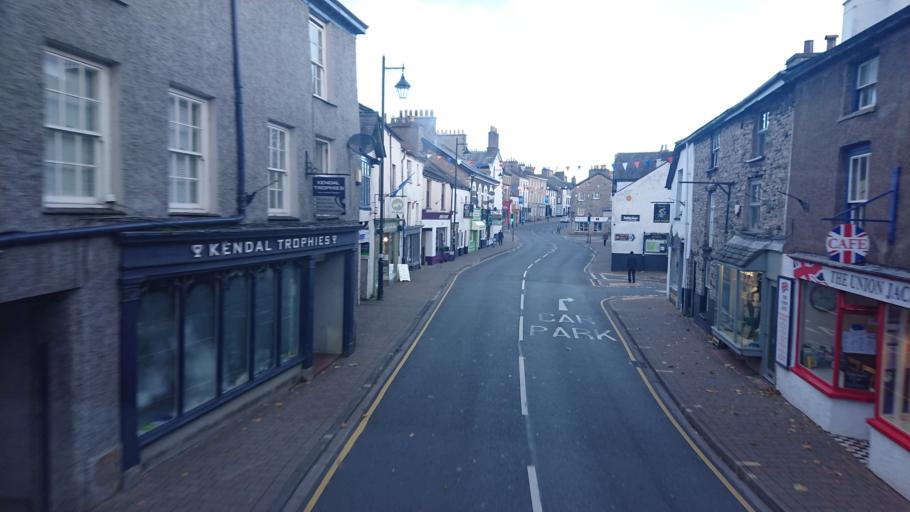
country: GB
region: England
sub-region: Cumbria
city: Kendal
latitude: 54.3227
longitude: -2.7464
